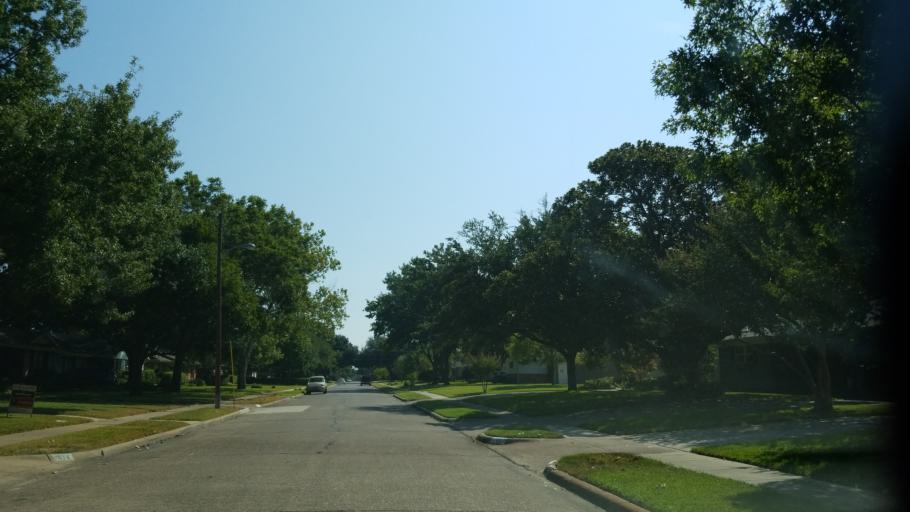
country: US
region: Texas
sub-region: Dallas County
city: Richardson
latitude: 32.9599
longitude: -96.7416
